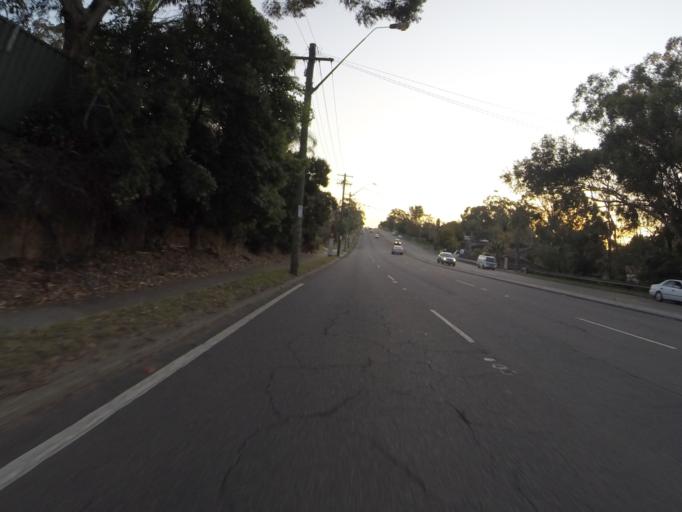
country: AU
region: New South Wales
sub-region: Hurstville
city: Peakhurst
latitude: -33.9642
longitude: 151.0405
